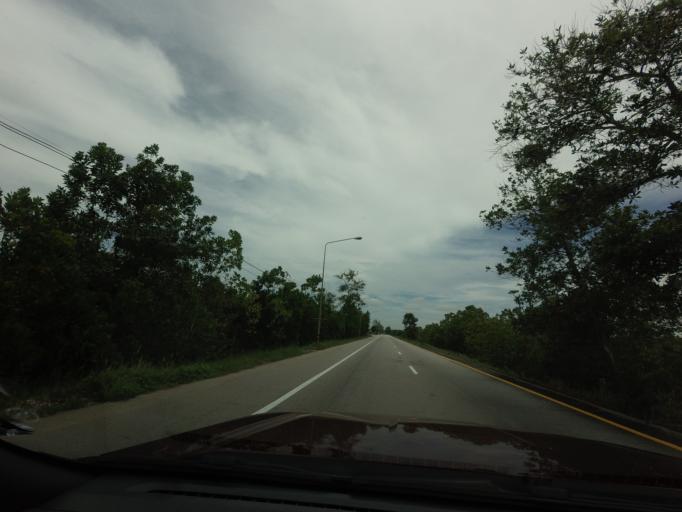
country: TH
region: Narathiwat
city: Narathiwat
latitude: 6.3452
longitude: 101.8724
